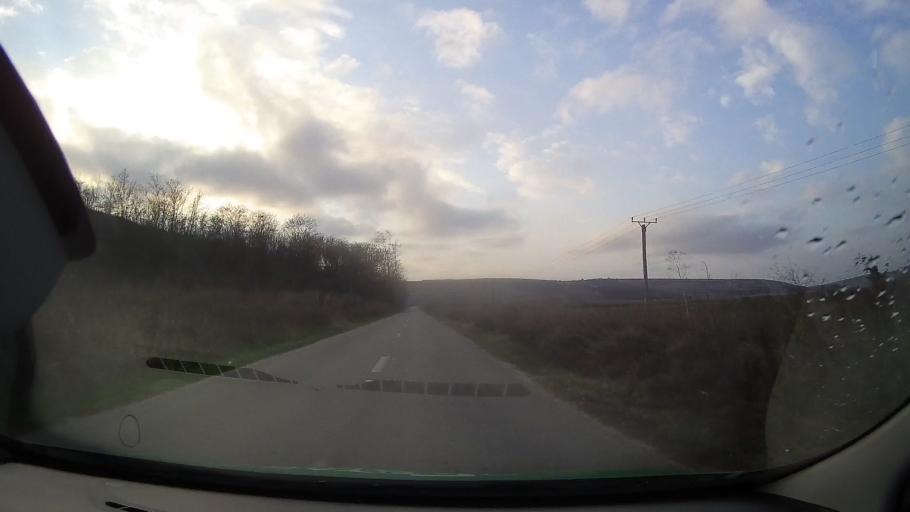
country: RO
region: Constanta
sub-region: Comuna Dobromir
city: Dobromir
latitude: 44.0352
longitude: 27.8494
